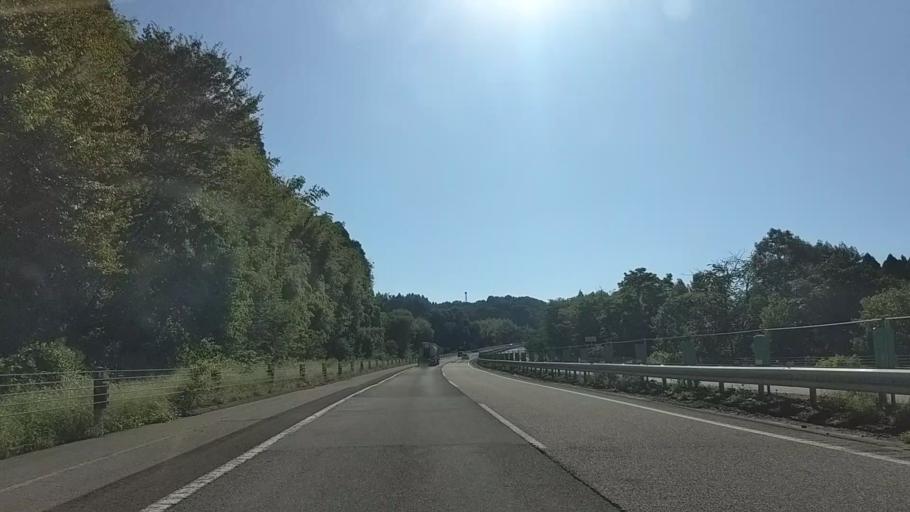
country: JP
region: Ishikawa
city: Tsubata
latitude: 36.6029
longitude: 136.7262
